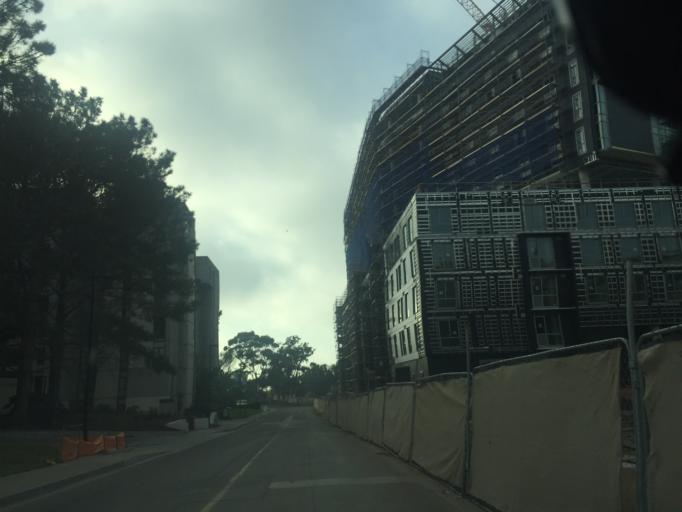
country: US
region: California
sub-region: San Diego County
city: La Jolla
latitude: 32.8797
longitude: -117.2421
